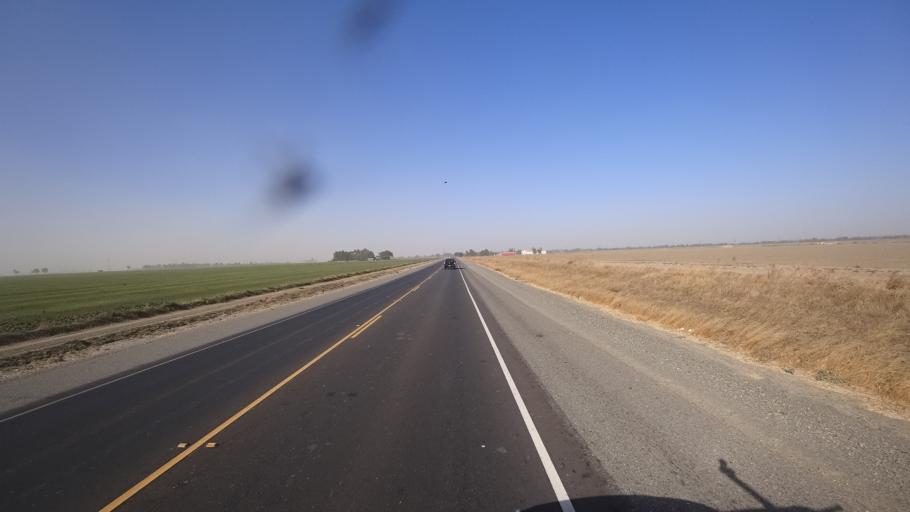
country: US
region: California
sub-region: Yolo County
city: Woodland
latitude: 38.7713
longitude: -121.7287
